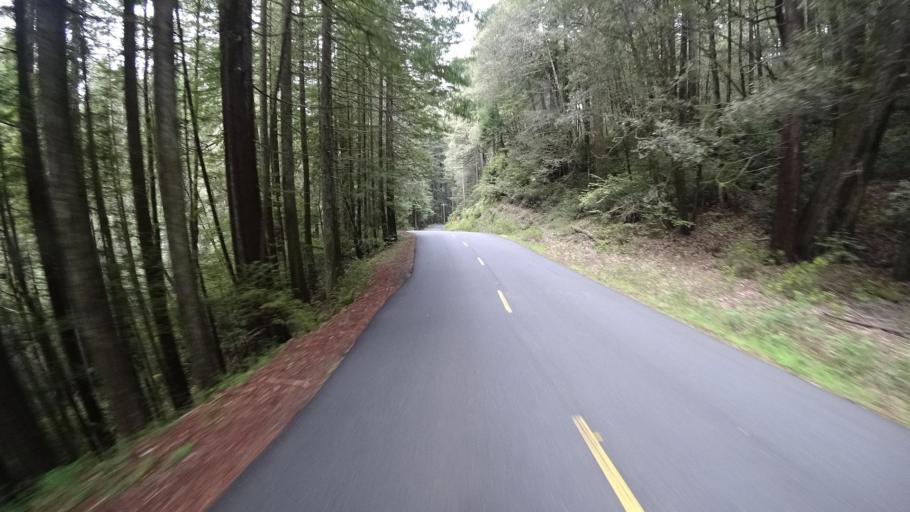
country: US
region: California
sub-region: Humboldt County
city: Redway
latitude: 40.2800
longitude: -123.8504
